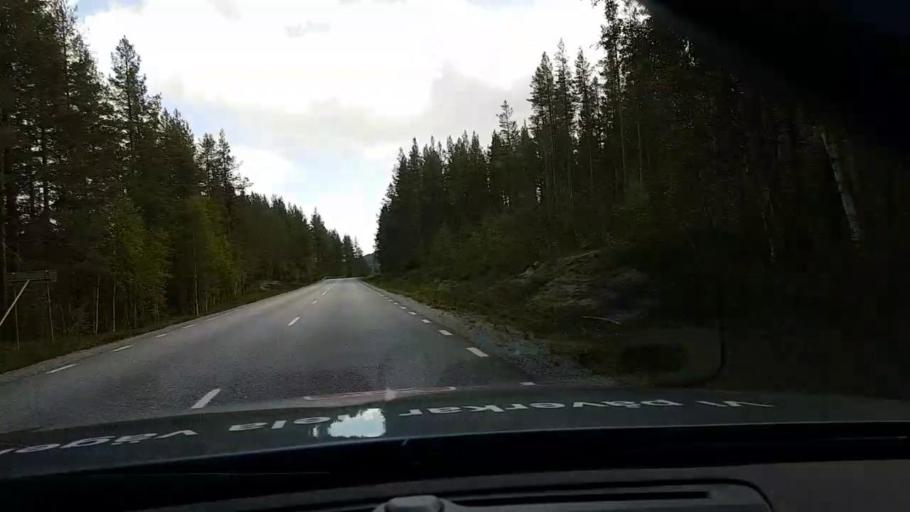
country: SE
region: Vaesternorrland
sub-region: OErnskoeldsviks Kommun
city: Bredbyn
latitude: 63.6925
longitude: 17.7680
